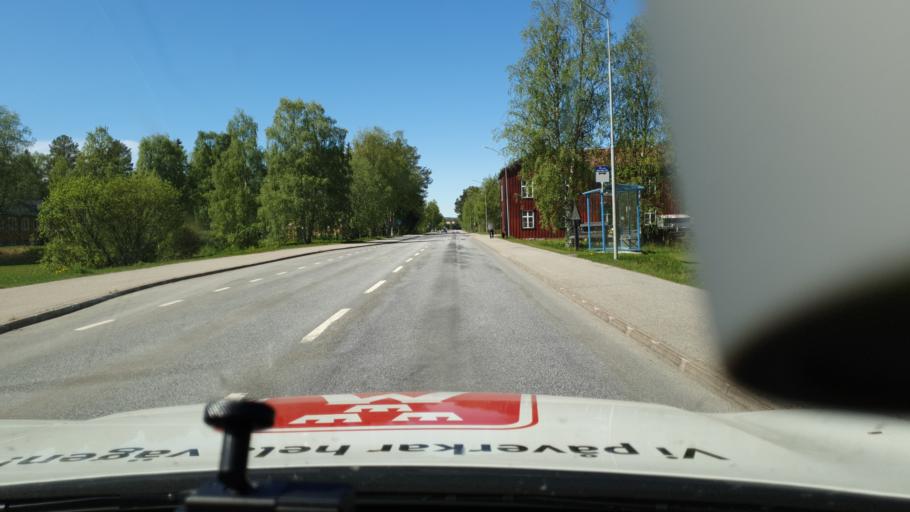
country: SE
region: Vaesterbotten
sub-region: Storumans Kommun
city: Storuman
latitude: 65.0641
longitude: 17.1708
